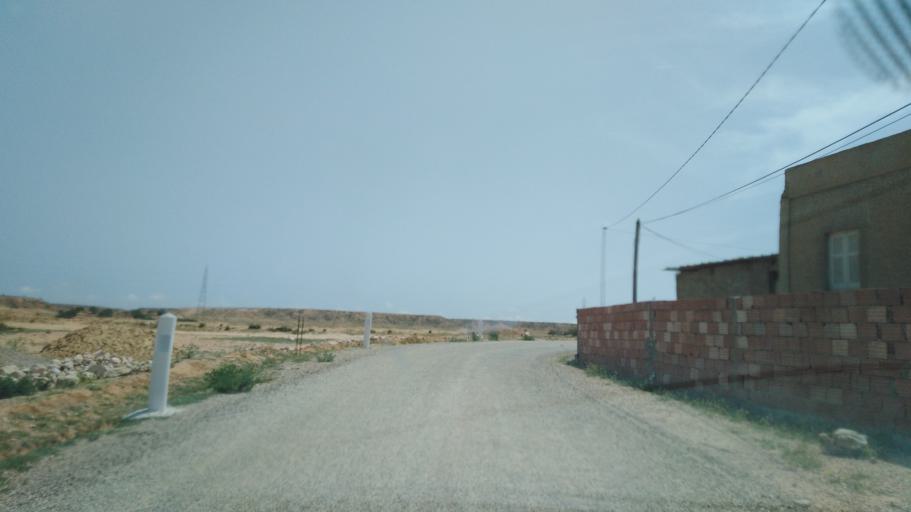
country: TN
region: Safaqis
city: Sfax
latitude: 34.7270
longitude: 10.5539
